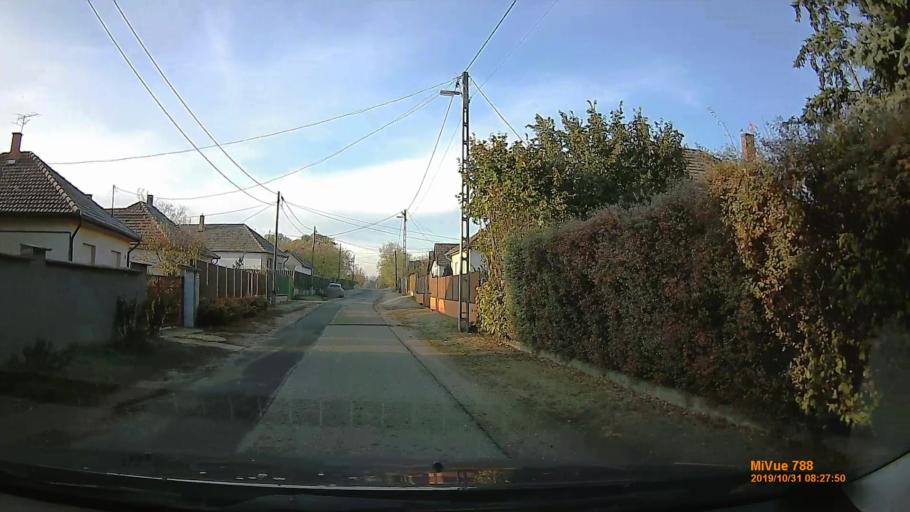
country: HU
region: Pest
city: Tapiobicske
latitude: 47.3607
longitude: 19.6814
